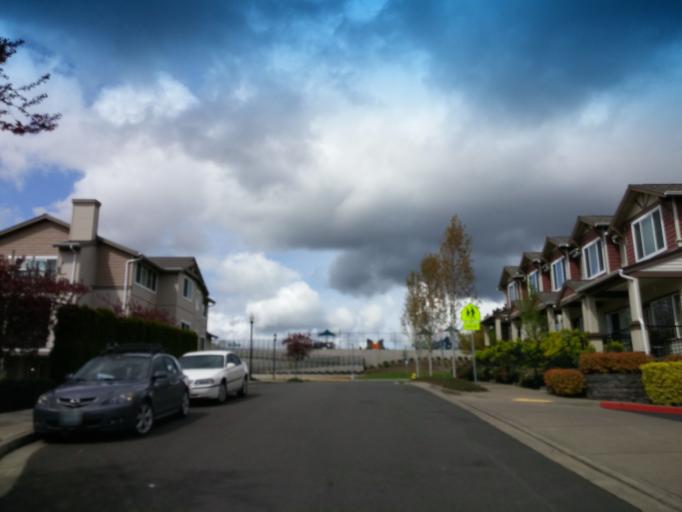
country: US
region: Oregon
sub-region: Washington County
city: Cedar Mill
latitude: 45.5224
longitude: -122.7963
